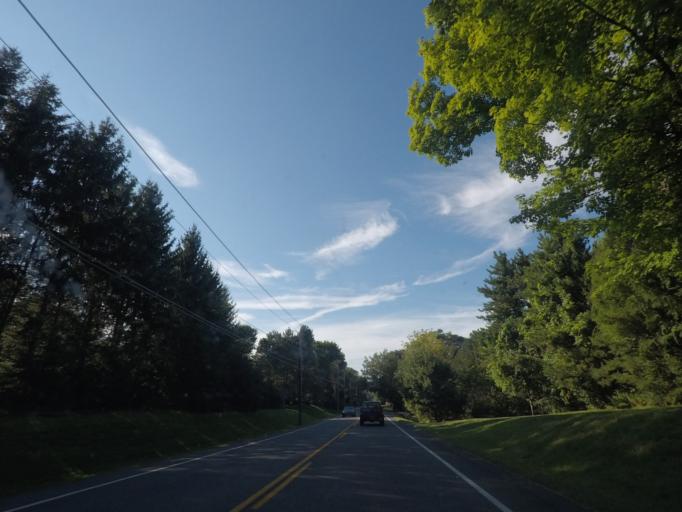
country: US
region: New York
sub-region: Albany County
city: West Albany
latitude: 42.7146
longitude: -73.7646
